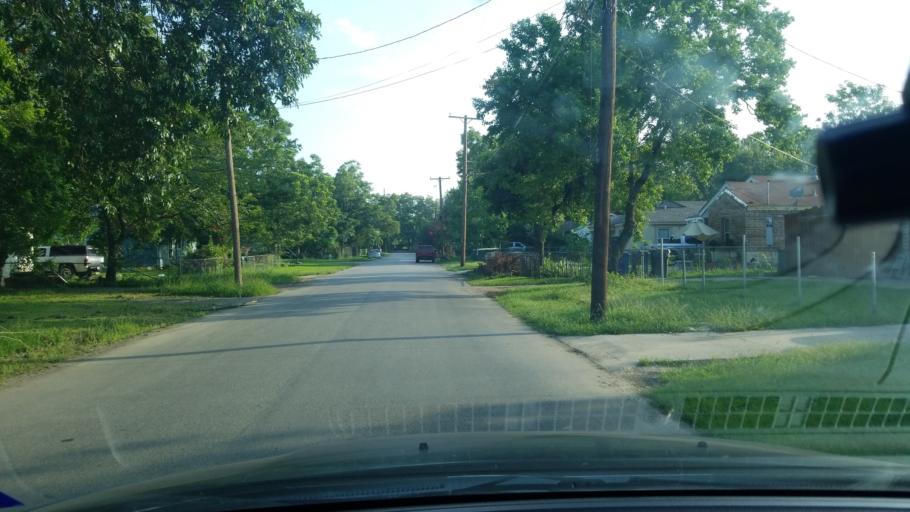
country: US
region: Texas
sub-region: Dallas County
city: Balch Springs
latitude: 32.7179
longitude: -96.6751
